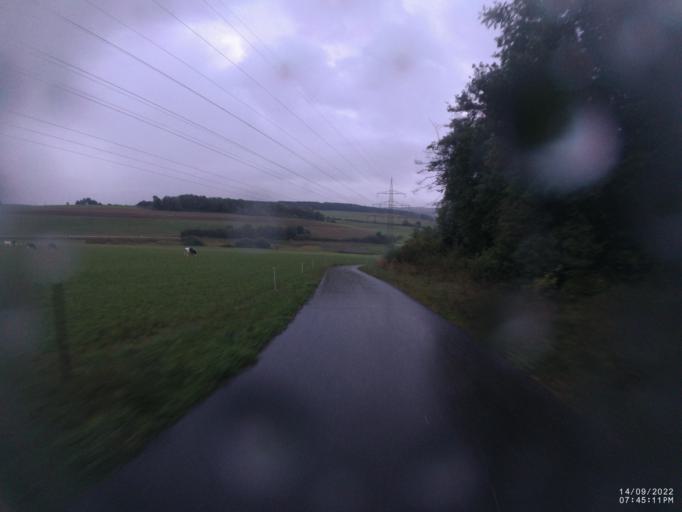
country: DE
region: Rheinland-Pfalz
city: Nohn
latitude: 50.3243
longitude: 6.7798
